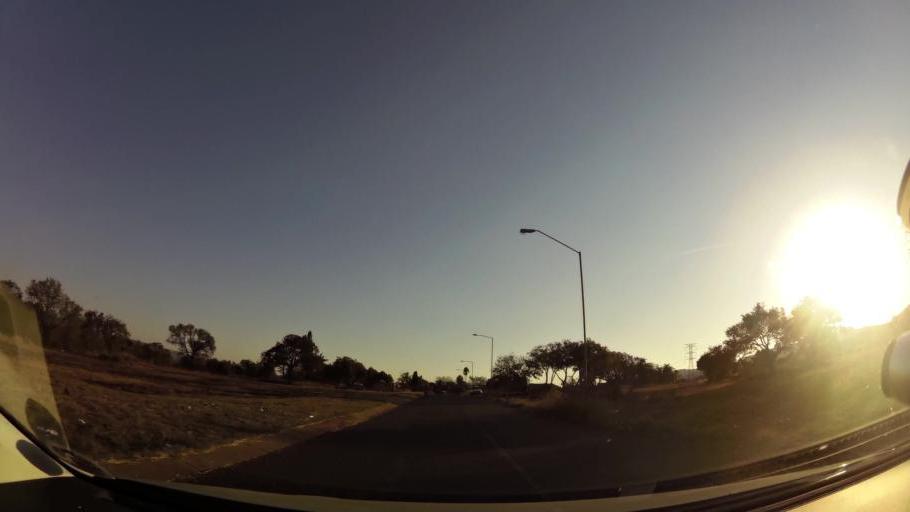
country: ZA
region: Gauteng
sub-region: City of Tshwane Metropolitan Municipality
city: Pretoria
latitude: -25.7369
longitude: 28.1133
